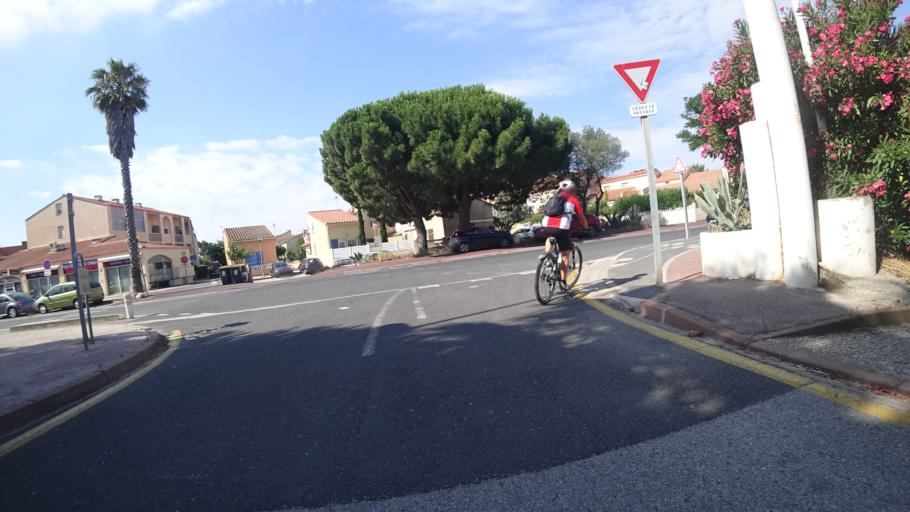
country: FR
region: Languedoc-Roussillon
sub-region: Departement des Pyrenees-Orientales
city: Canet-en-Roussillon
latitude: 42.7014
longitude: 3.0308
